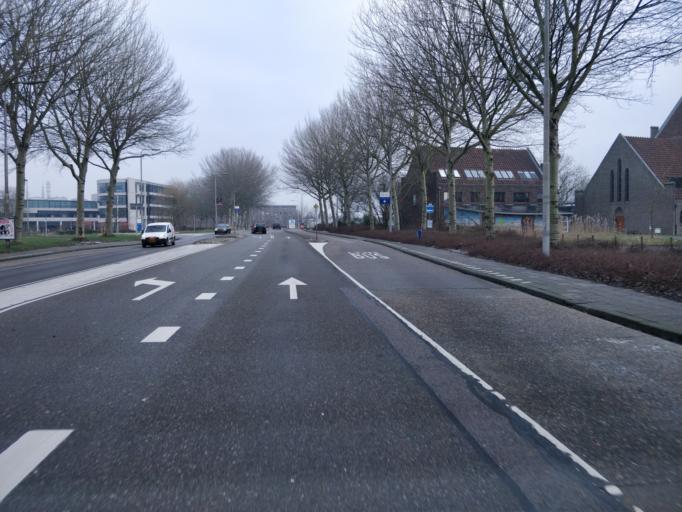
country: NL
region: Friesland
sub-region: Gemeente Leeuwarden
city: Leeuwarden
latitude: 53.1945
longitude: 5.8015
